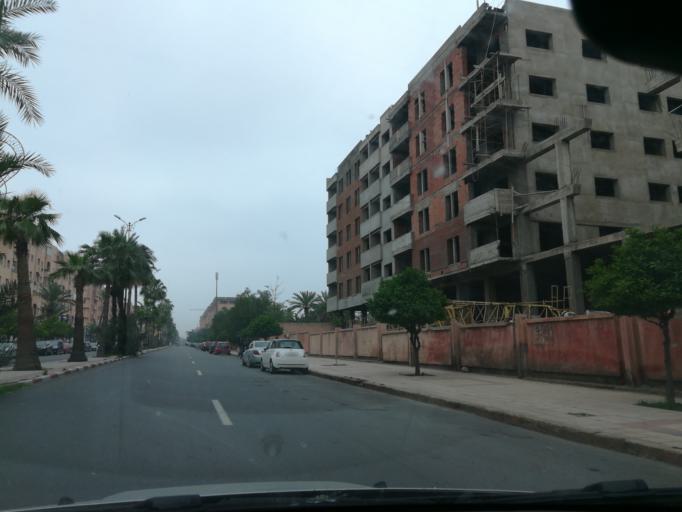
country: MA
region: Marrakech-Tensift-Al Haouz
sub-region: Marrakech
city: Marrakesh
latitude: 31.6607
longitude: -8.0069
